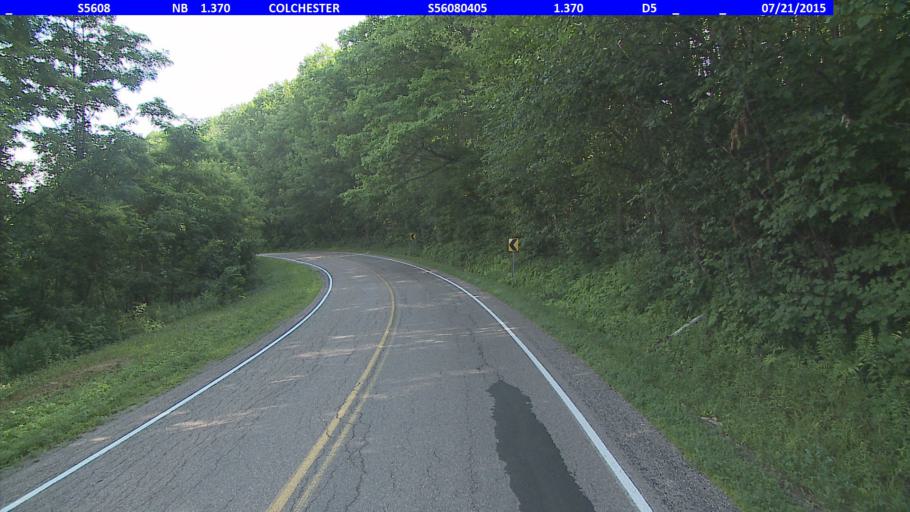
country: US
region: Vermont
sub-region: Chittenden County
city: Winooski
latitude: 44.5182
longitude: -73.2010
